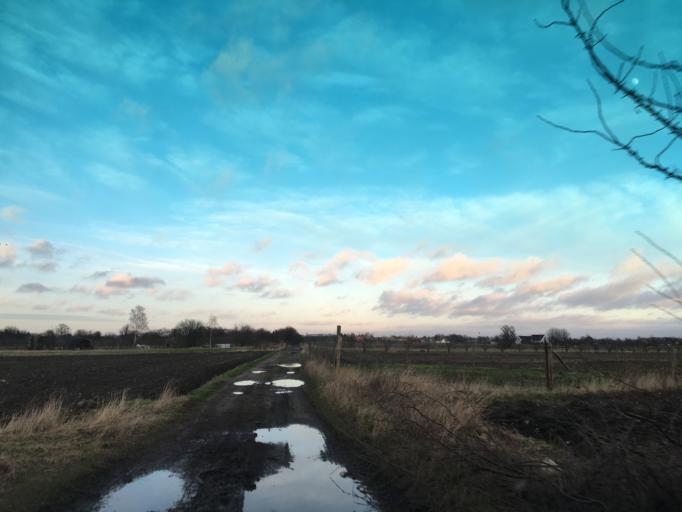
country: DK
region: Capital Region
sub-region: Dragor Kommune
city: Dragor
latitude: 55.5874
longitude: 12.6227
